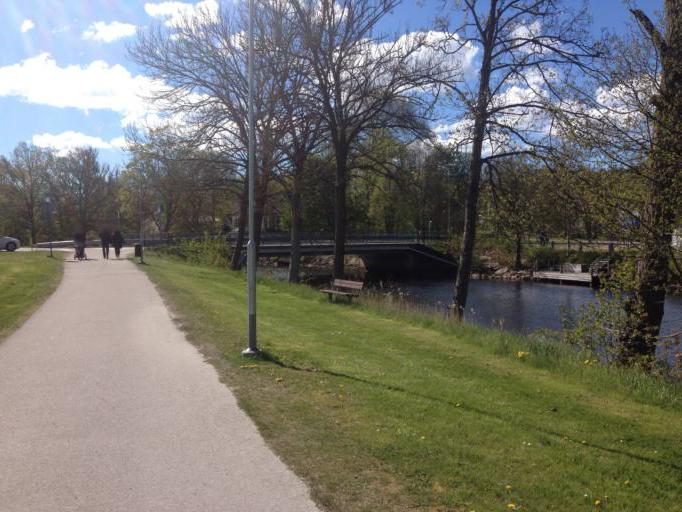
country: SE
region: Blekinge
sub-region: Ronneby Kommun
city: Ronneby
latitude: 56.2007
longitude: 15.2859
